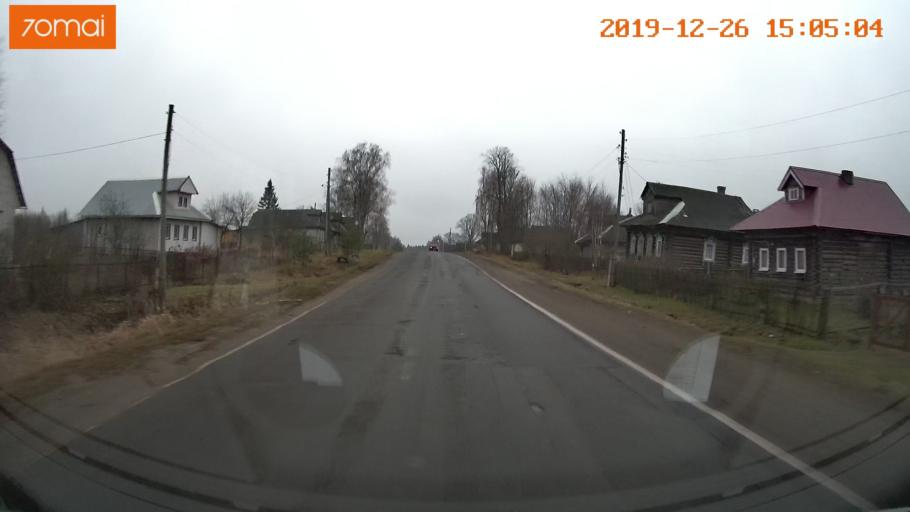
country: RU
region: Jaroslavl
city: Rybinsk
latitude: 58.1930
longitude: 38.8552
